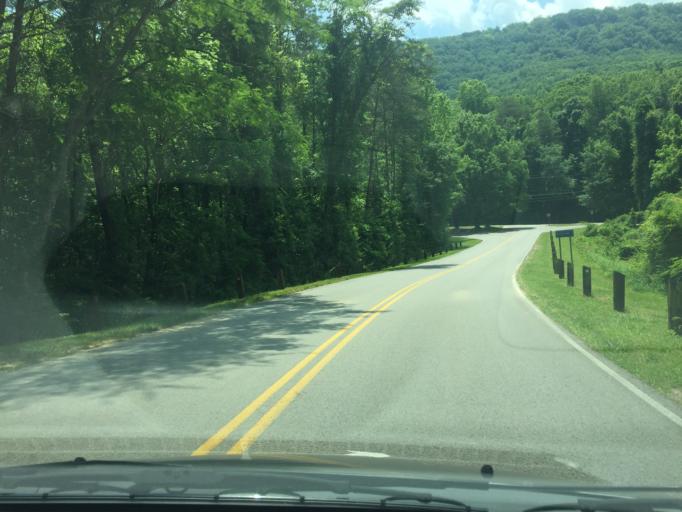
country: US
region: Tennessee
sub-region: Hamilton County
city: Lookout Mountain
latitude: 35.0381
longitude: -85.4179
